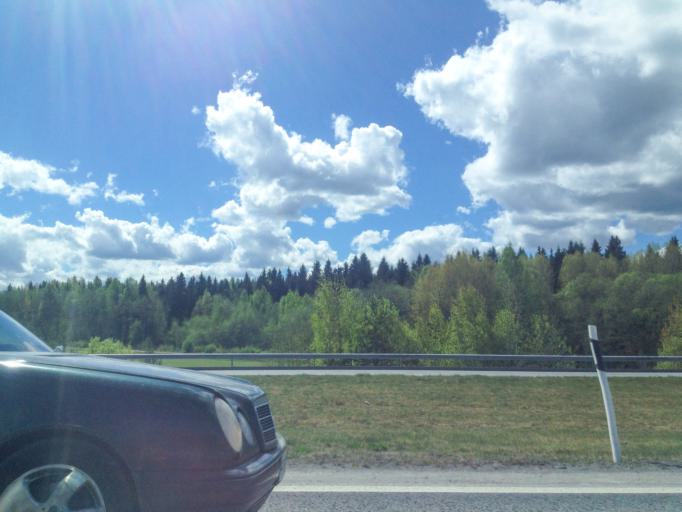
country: FI
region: Haeme
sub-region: Haemeenlinna
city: Parola
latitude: 61.0344
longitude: 24.3870
